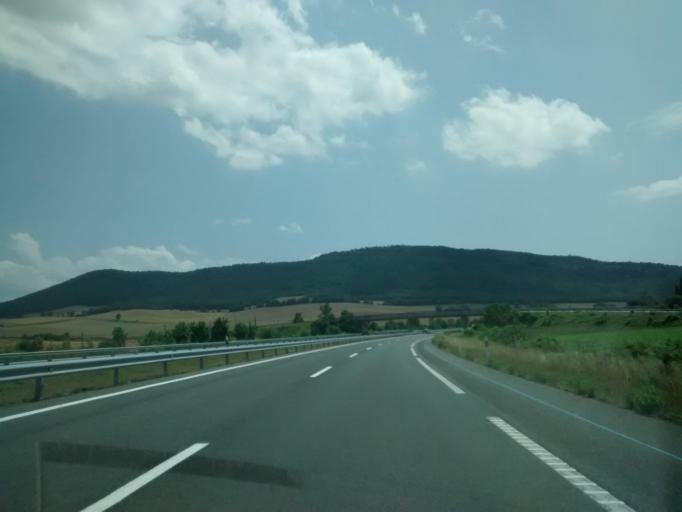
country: ES
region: Basque Country
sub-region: Provincia de Alava
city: Arminon
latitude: 42.7917
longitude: -2.8998
